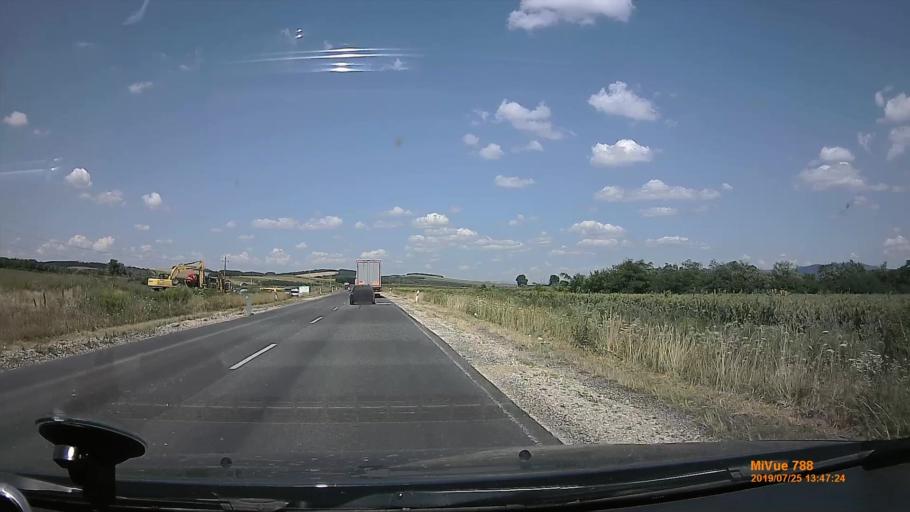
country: HU
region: Borsod-Abauj-Zemplen
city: Gonc
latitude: 48.4966
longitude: 21.2192
